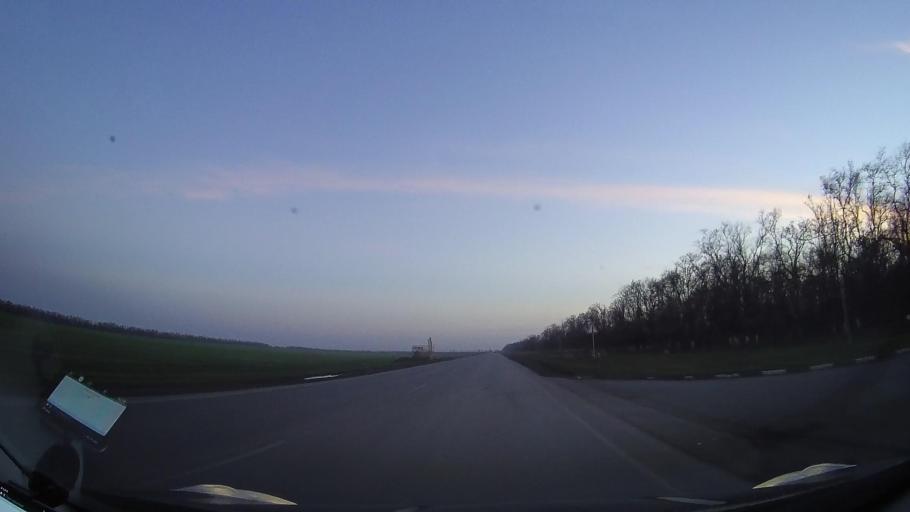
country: RU
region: Rostov
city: Zernograd
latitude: 46.8311
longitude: 40.2994
